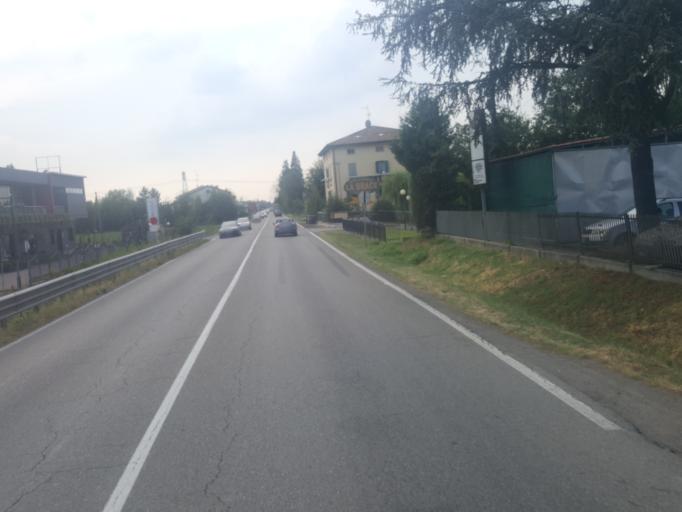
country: IT
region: Emilia-Romagna
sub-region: Provincia di Modena
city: San Damaso
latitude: 44.6208
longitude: 10.9872
